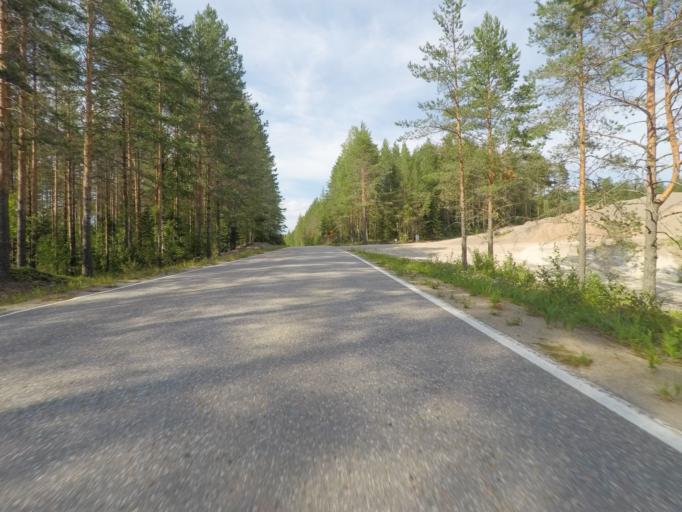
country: FI
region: Southern Savonia
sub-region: Savonlinna
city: Sulkava
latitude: 61.7878
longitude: 28.2433
